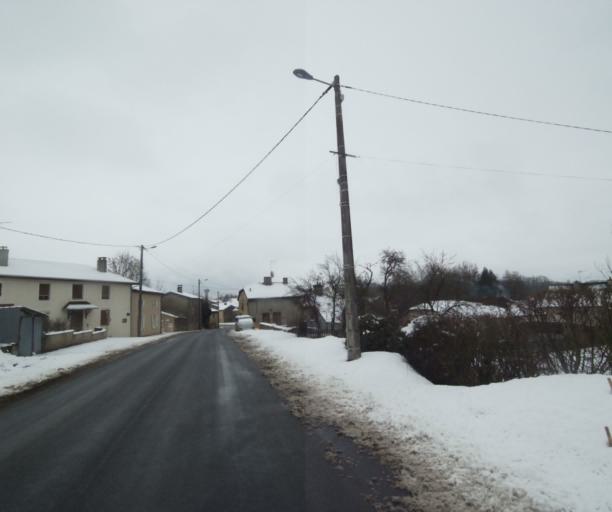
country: FR
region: Champagne-Ardenne
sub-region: Departement de la Haute-Marne
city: Wassy
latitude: 48.4406
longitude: 4.9567
